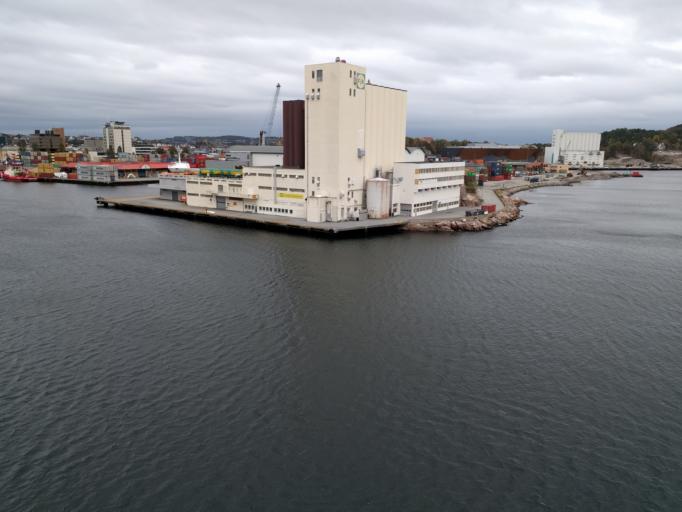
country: NO
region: Vest-Agder
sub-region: Kristiansand
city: Kristiansand
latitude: 58.1400
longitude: 7.9865
